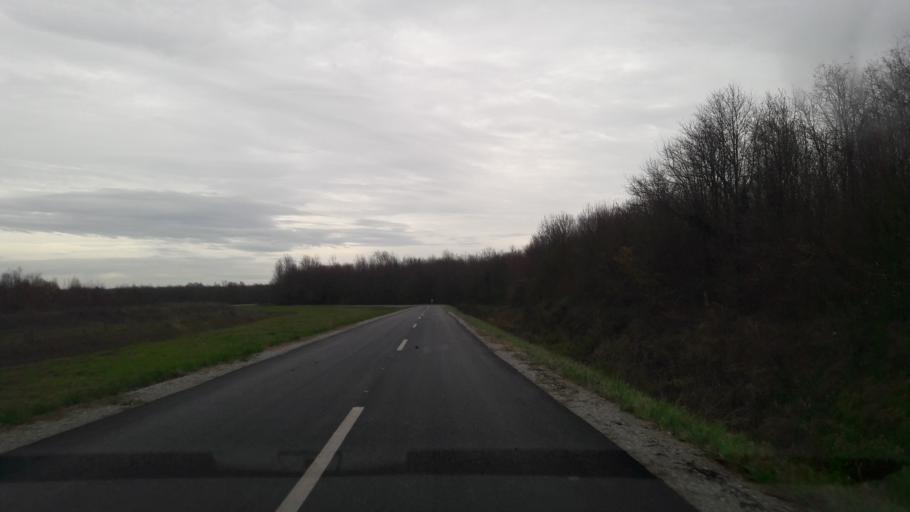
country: HR
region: Osjecko-Baranjska
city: Velimirovac
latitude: 45.6214
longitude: 18.0789
